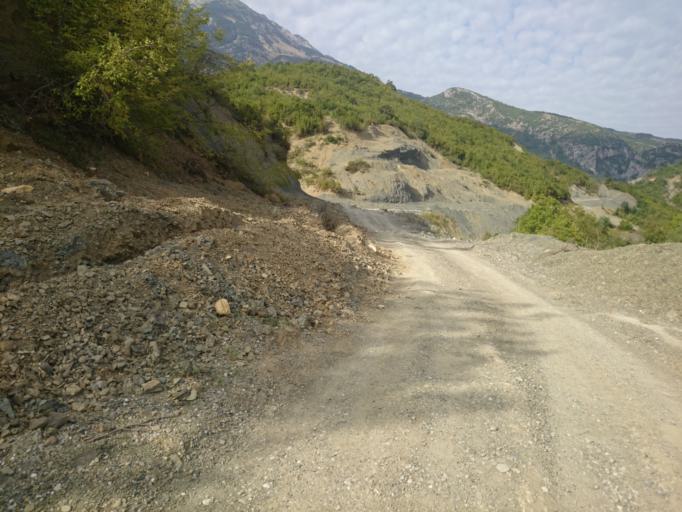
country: AL
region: Elbasan
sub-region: Rrethi i Gramshit
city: Kushove
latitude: 40.7576
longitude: 20.1886
